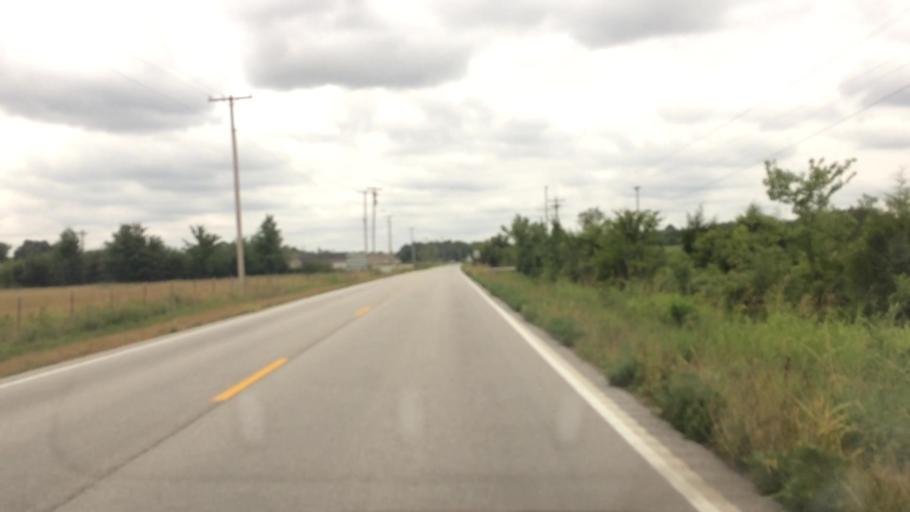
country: US
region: Missouri
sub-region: Greene County
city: Strafford
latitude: 37.2862
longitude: -93.1131
